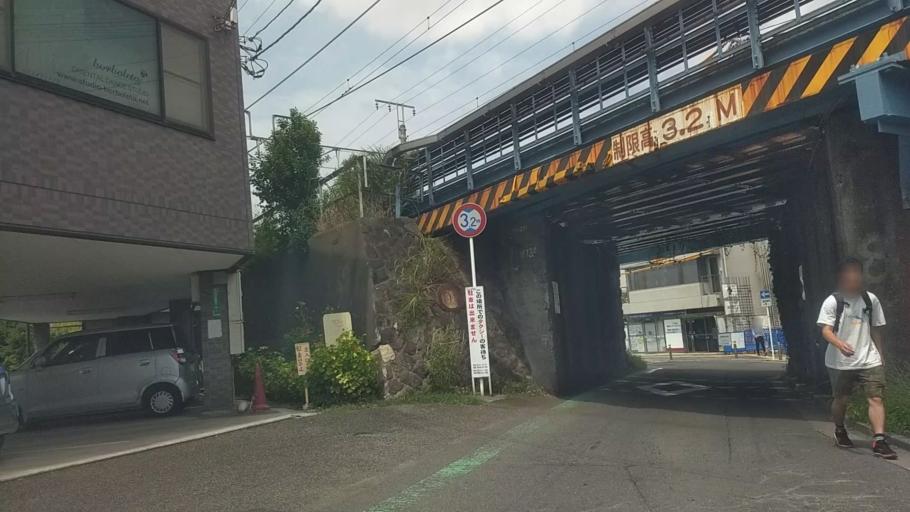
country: JP
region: Kanagawa
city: Yokohama
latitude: 35.5089
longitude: 139.6332
